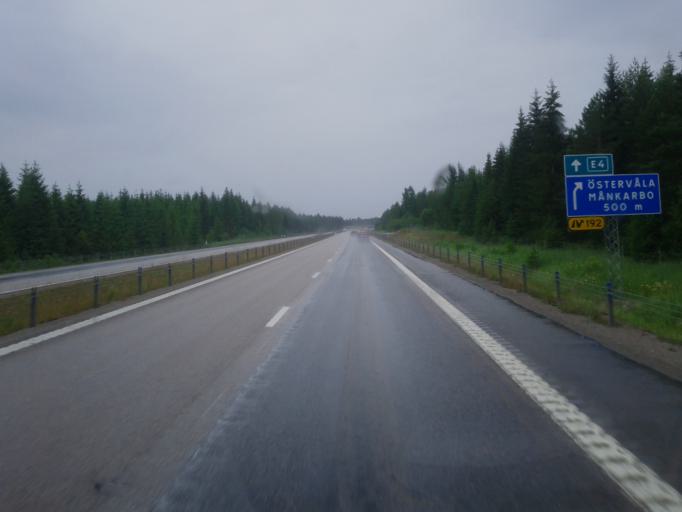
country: SE
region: Uppsala
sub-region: Tierps Kommun
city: Tierp
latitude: 60.2039
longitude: 17.4968
